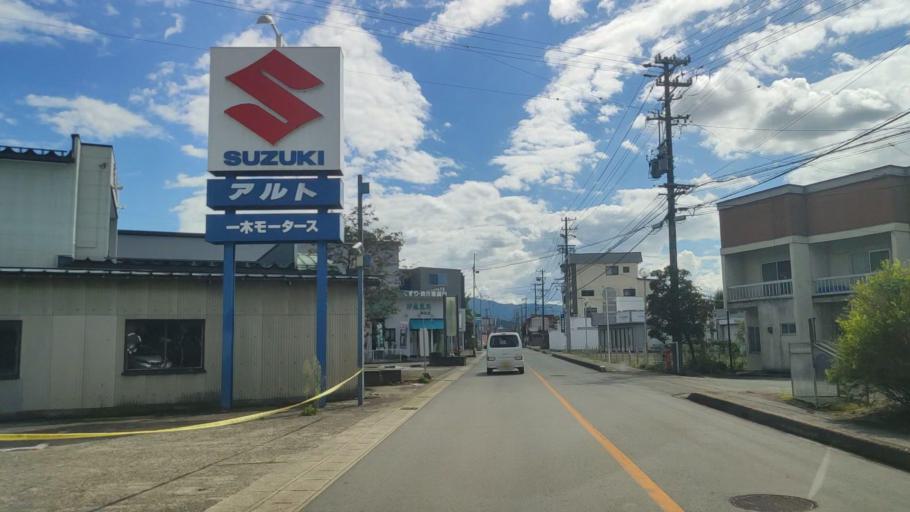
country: JP
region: Gifu
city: Takayama
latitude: 36.1608
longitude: 137.2522
